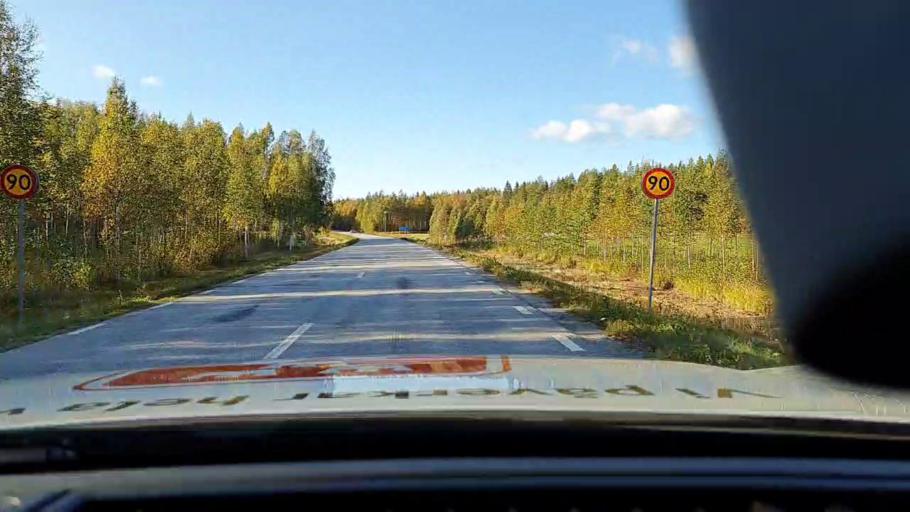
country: SE
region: Norrbotten
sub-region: Pitea Kommun
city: Norrfjarden
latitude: 65.4332
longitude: 21.4859
